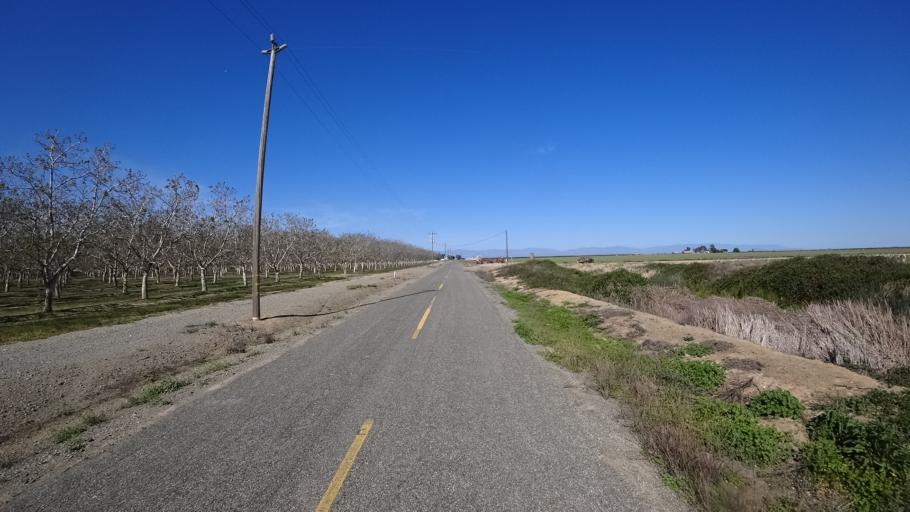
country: US
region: California
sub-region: Glenn County
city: Willows
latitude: 39.6112
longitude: -122.1434
